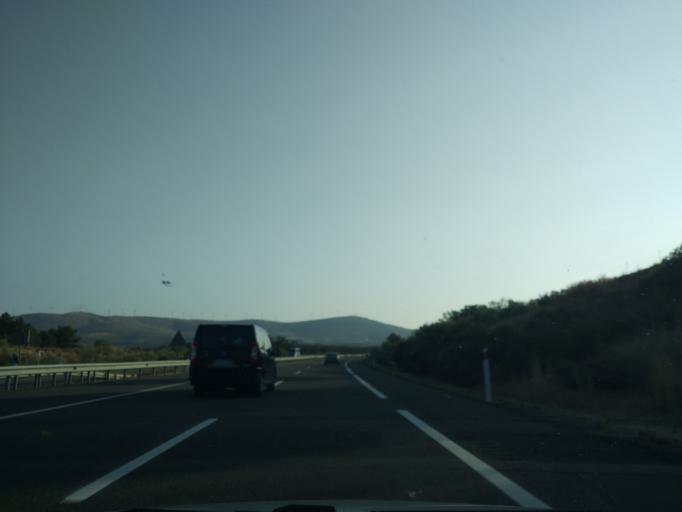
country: ES
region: Castille and Leon
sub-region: Provincia de Segovia
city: Villacastin
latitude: 40.7617
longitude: -4.4417
